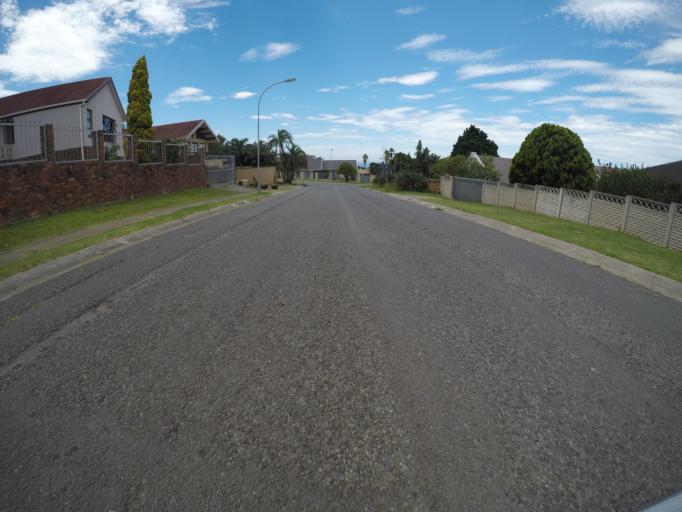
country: ZA
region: Eastern Cape
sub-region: Buffalo City Metropolitan Municipality
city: East London
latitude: -33.0379
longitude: 27.8625
